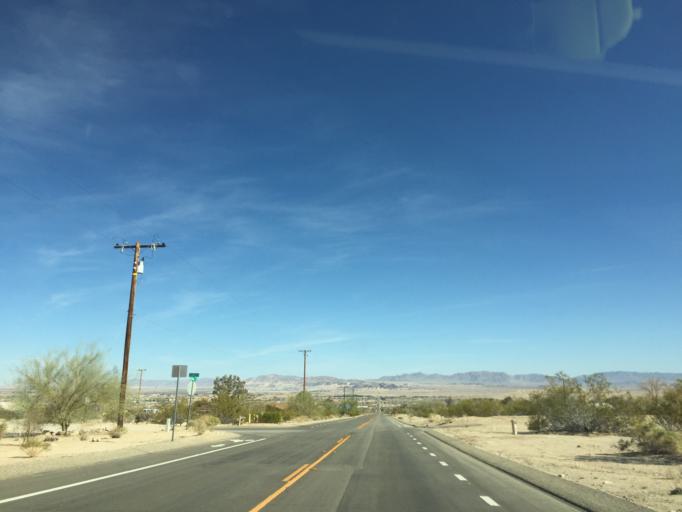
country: US
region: California
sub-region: San Bernardino County
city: Twentynine Palms
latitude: 34.1099
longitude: -116.0367
